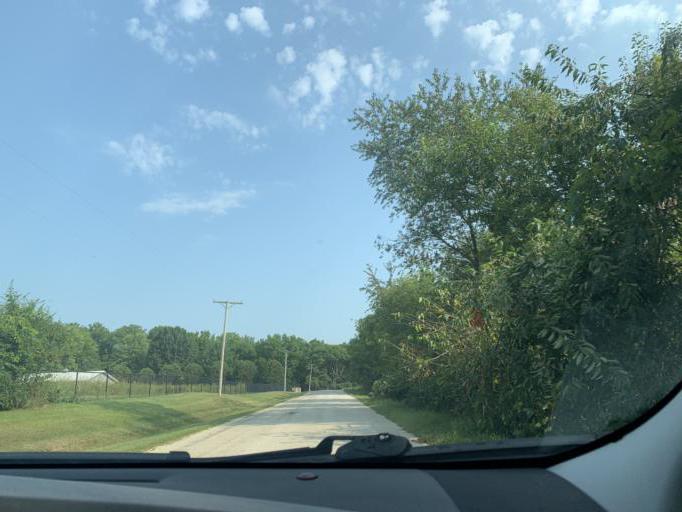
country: US
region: Illinois
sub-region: Whiteside County
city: Morrison
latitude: 41.8751
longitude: -89.9304
